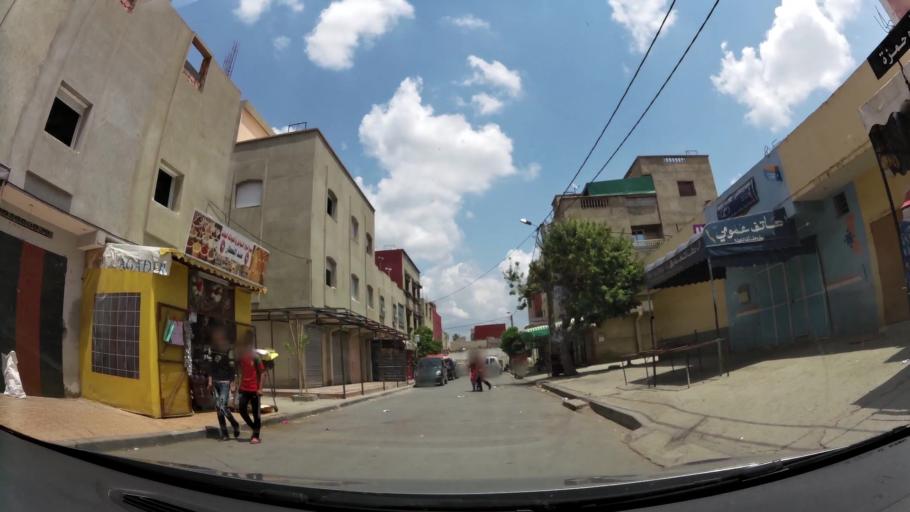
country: MA
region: Rabat-Sale-Zemmour-Zaer
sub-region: Khemisset
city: Tiflet
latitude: 34.0039
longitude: -6.5308
